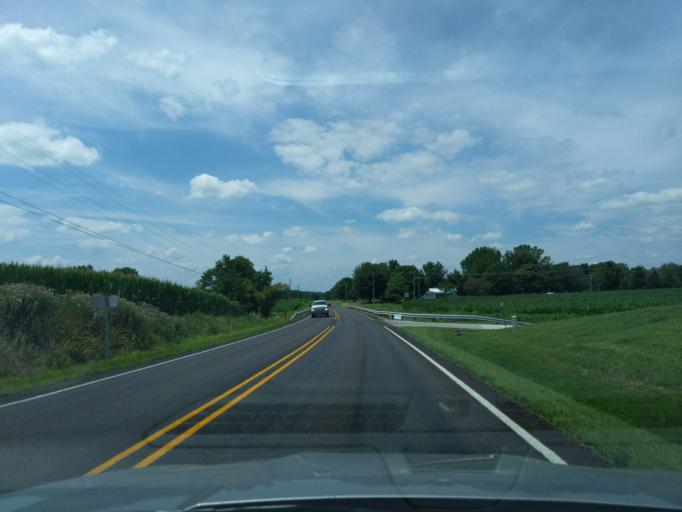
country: US
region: Indiana
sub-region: Decatur County
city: Greensburg
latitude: 39.2630
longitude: -85.3757
